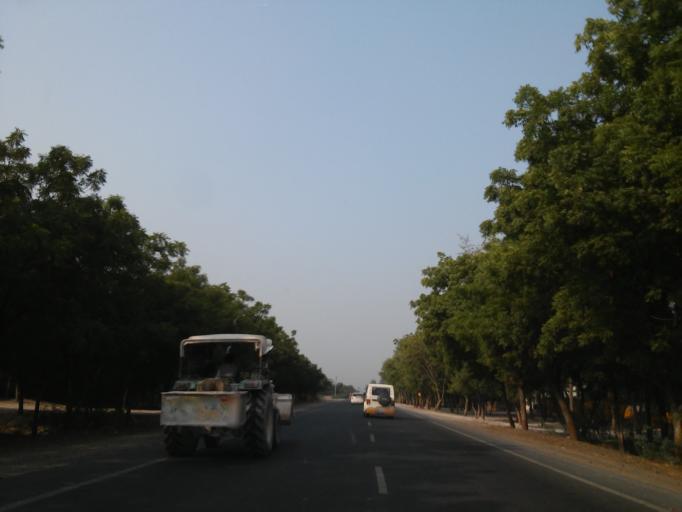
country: IN
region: Gujarat
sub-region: Kachchh
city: Bhuj
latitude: 23.2396
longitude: 69.8054
